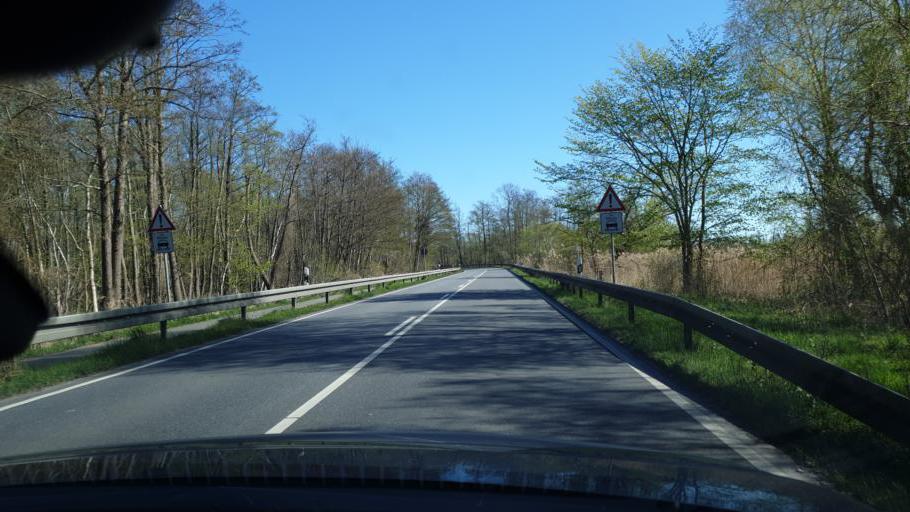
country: DE
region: Mecklenburg-Vorpommern
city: Werdervorstadt
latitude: 53.6609
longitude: 11.4472
